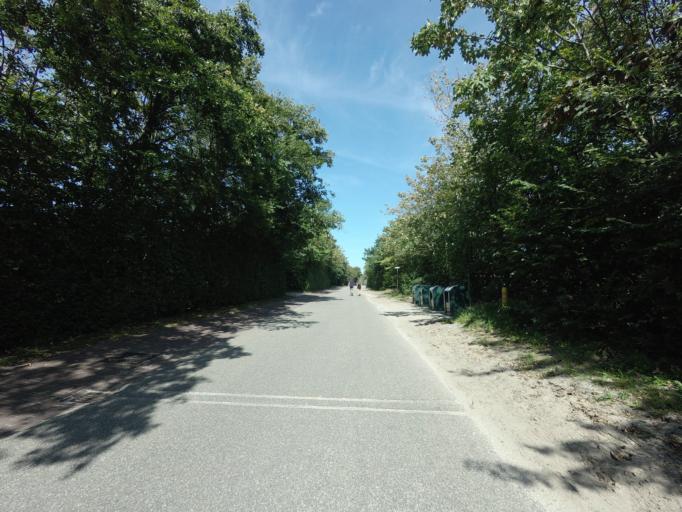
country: NL
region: Friesland
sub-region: Gemeente Ameland
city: Hollum
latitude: 53.4484
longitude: 5.6365
